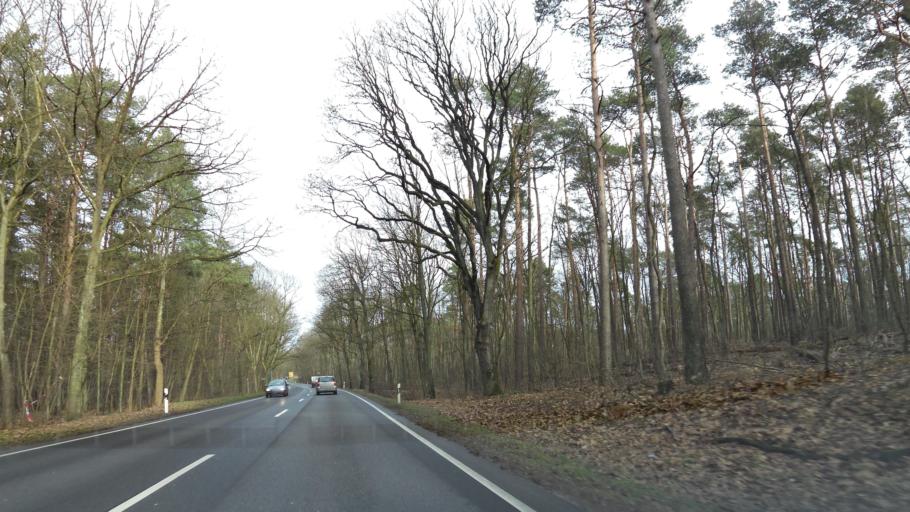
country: DE
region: Brandenburg
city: Strausberg
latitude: 52.5545
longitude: 13.8545
